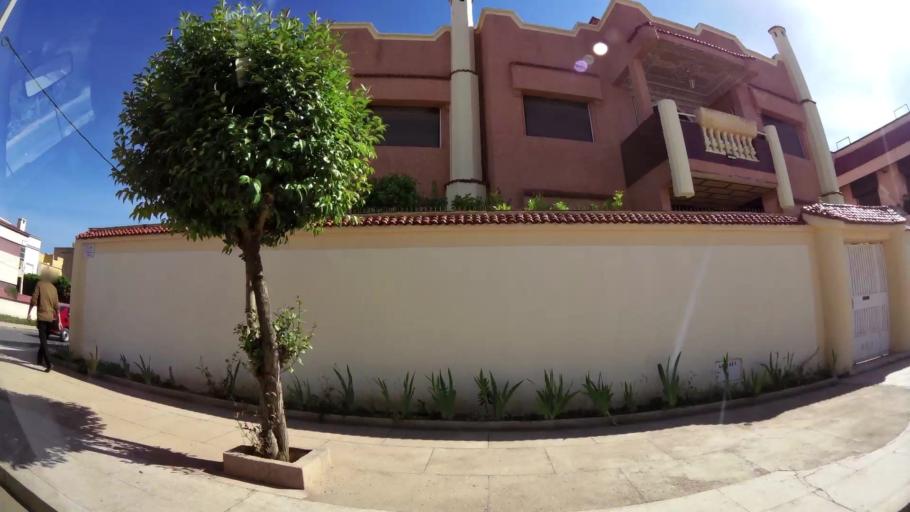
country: MA
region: Oriental
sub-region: Oujda-Angad
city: Oujda
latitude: 34.6621
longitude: -1.8955
